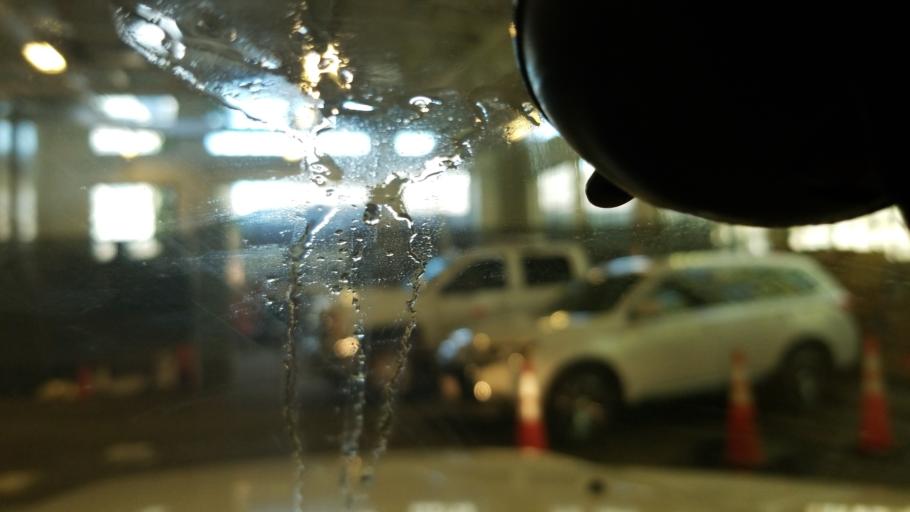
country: US
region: Washington, D.C.
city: Washington, D.C.
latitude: 38.9214
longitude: -77.0150
